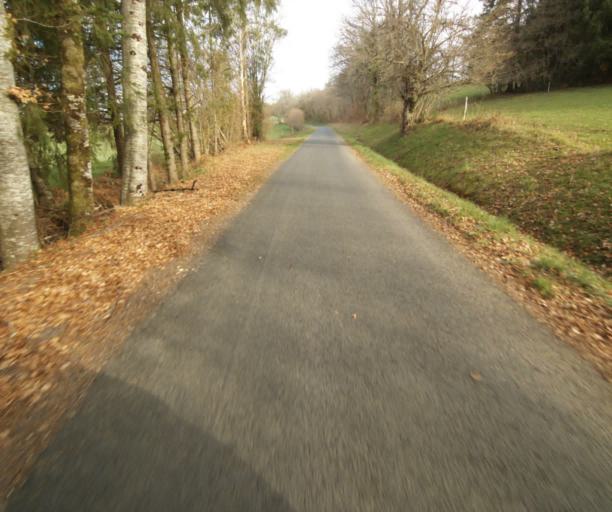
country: FR
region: Limousin
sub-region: Departement de la Correze
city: Chamboulive
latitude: 45.4466
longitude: 1.7561
